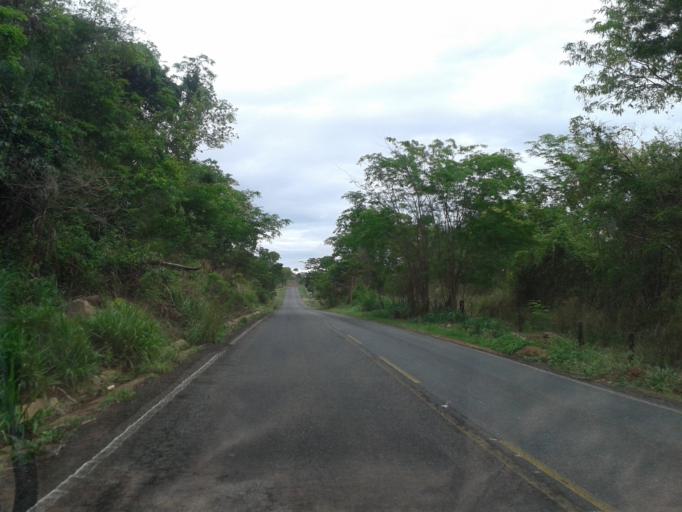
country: BR
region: Goias
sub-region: Caldas Novas
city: Caldas Novas
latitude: -18.0621
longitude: -48.6931
